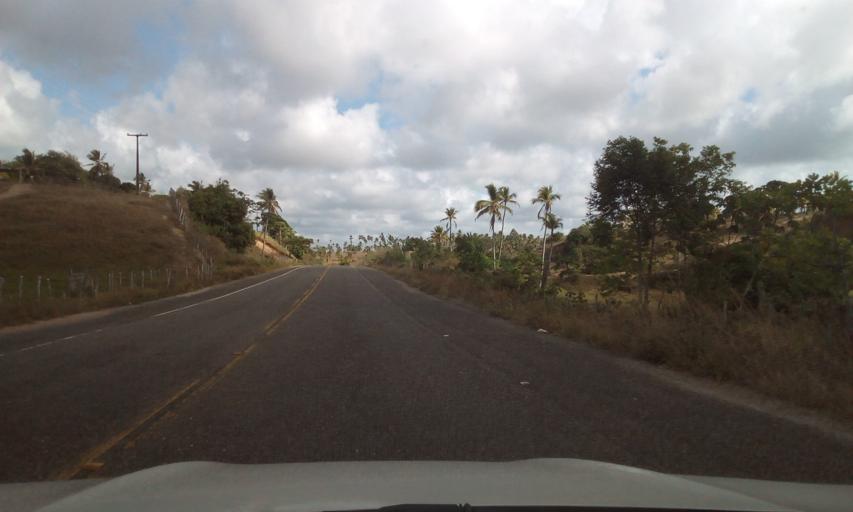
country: BR
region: Sergipe
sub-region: Indiaroba
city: Indiaroba
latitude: -11.4948
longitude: -37.4913
